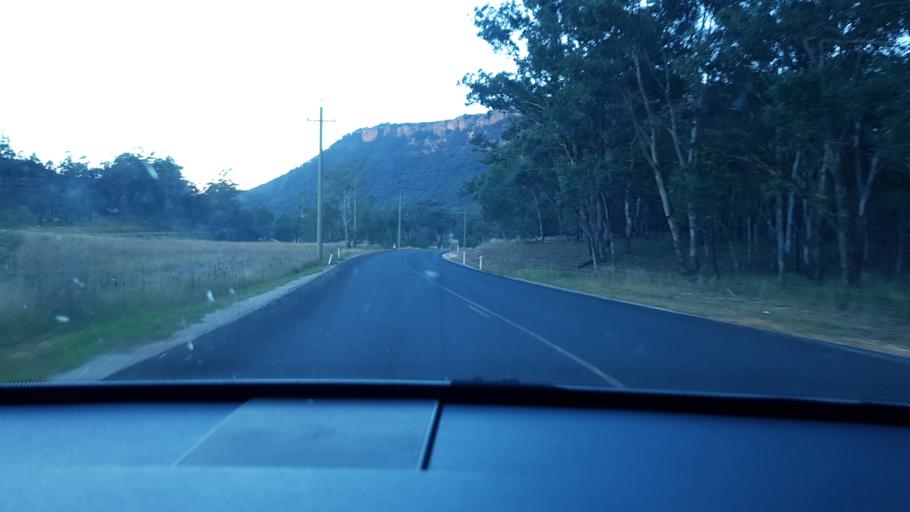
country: AU
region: New South Wales
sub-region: Lithgow
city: Portland
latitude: -33.2372
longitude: 150.1635
